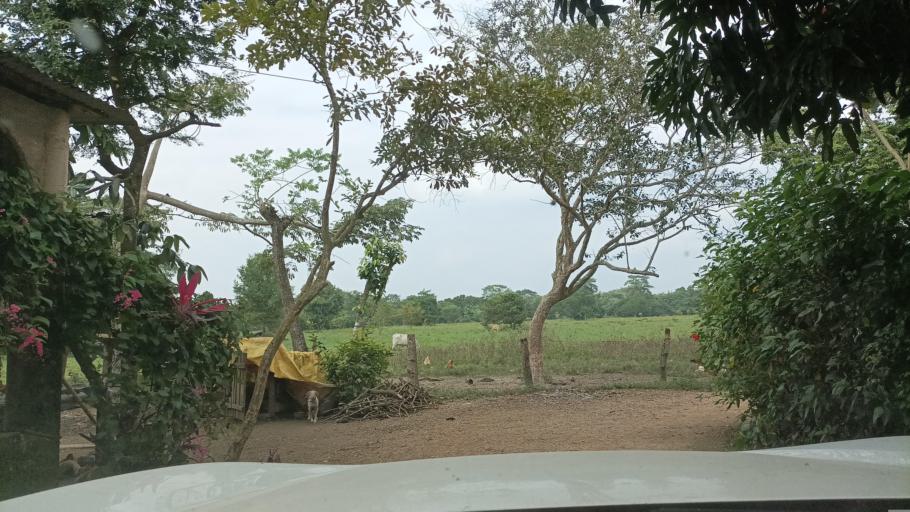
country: MX
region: Veracruz
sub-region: Texistepec
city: San Lorenzo Tenochtitlan
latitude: 17.7741
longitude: -94.8071
